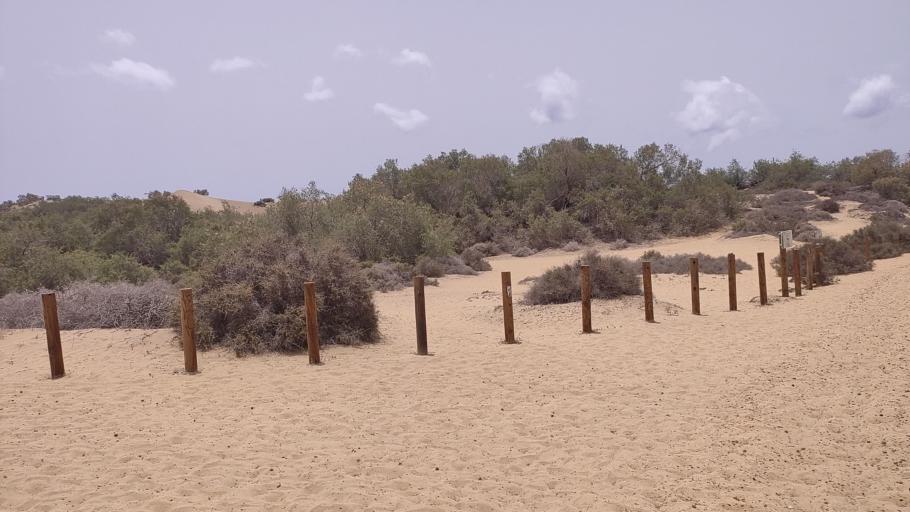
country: ES
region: Canary Islands
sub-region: Provincia de Las Palmas
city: Maspalomas
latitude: 27.7443
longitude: -15.5936
